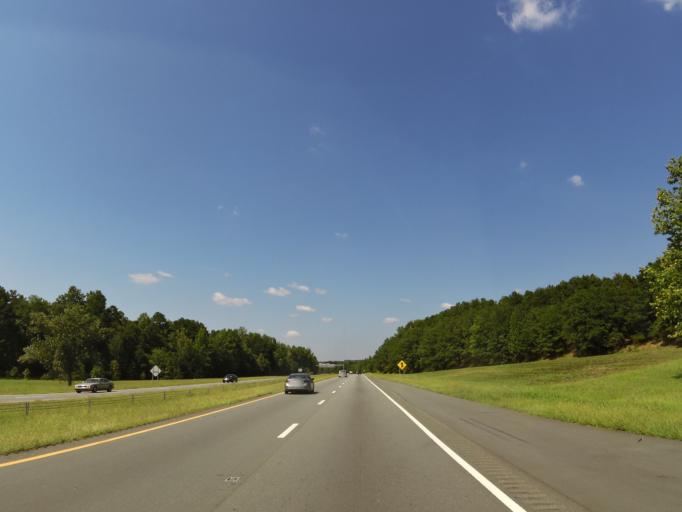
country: US
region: North Carolina
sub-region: Gaston County
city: Dallas
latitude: 35.3171
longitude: -81.1870
